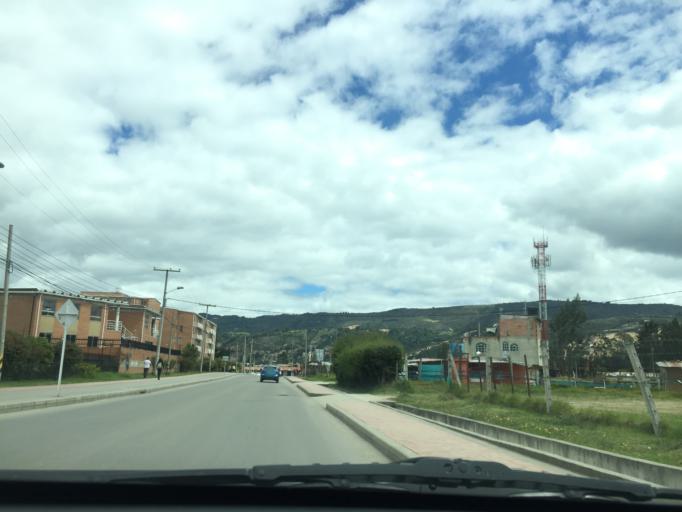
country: CO
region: Cundinamarca
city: Tocancipa
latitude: 4.9632
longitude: -73.9316
